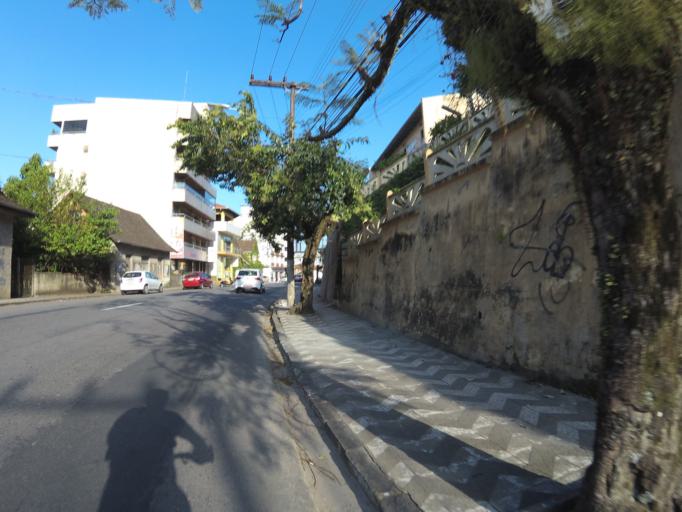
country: BR
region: Santa Catarina
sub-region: Blumenau
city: Blumenau
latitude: -26.9140
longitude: -49.0788
